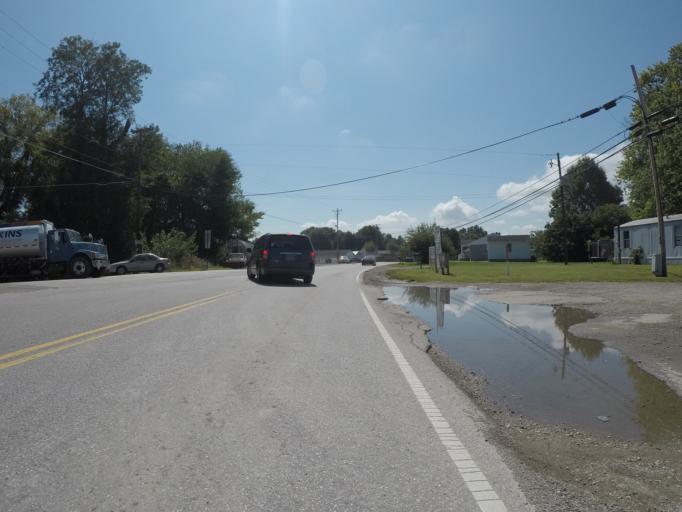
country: US
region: Ohio
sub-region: Lawrence County
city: South Point
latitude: 38.4515
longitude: -82.5939
